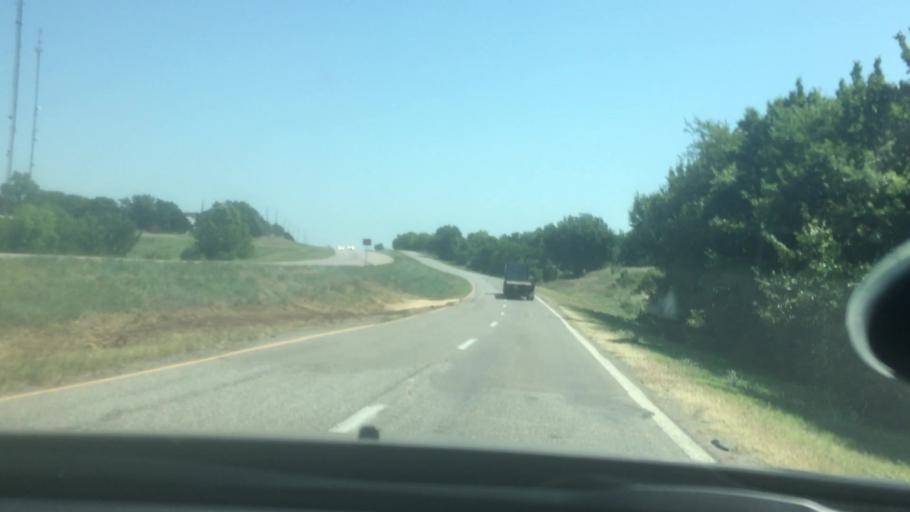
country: US
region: Oklahoma
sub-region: Pontotoc County
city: Ada
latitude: 34.7235
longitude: -96.7136
